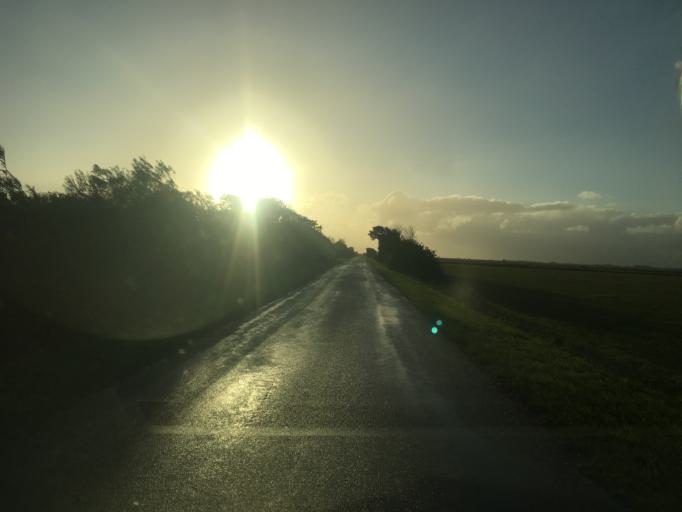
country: DE
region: Schleswig-Holstein
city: Aventoft
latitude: 54.9469
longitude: 8.7538
